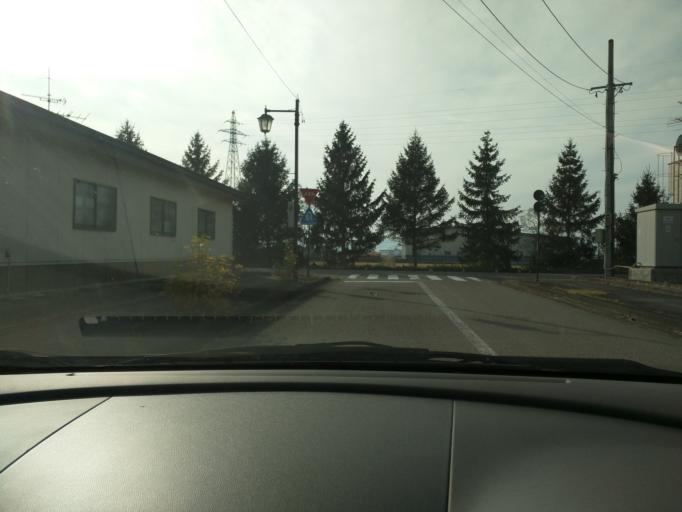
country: JP
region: Fukushima
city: Kitakata
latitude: 37.5207
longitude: 139.9137
